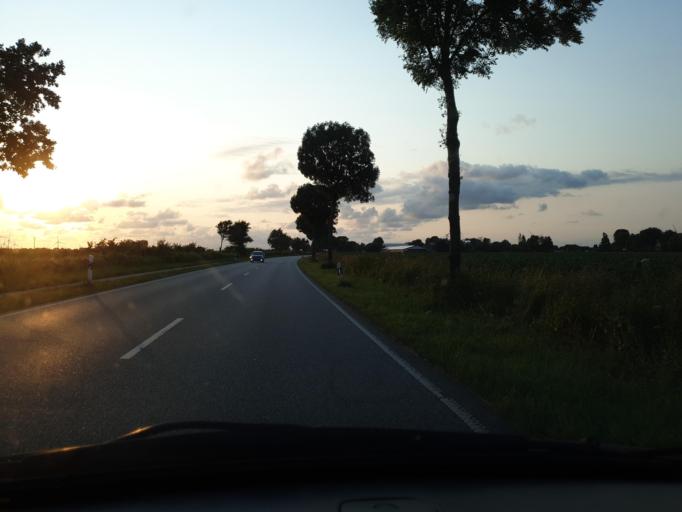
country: DE
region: Schleswig-Holstein
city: Schmedeswurth
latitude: 53.9116
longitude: 9.0545
